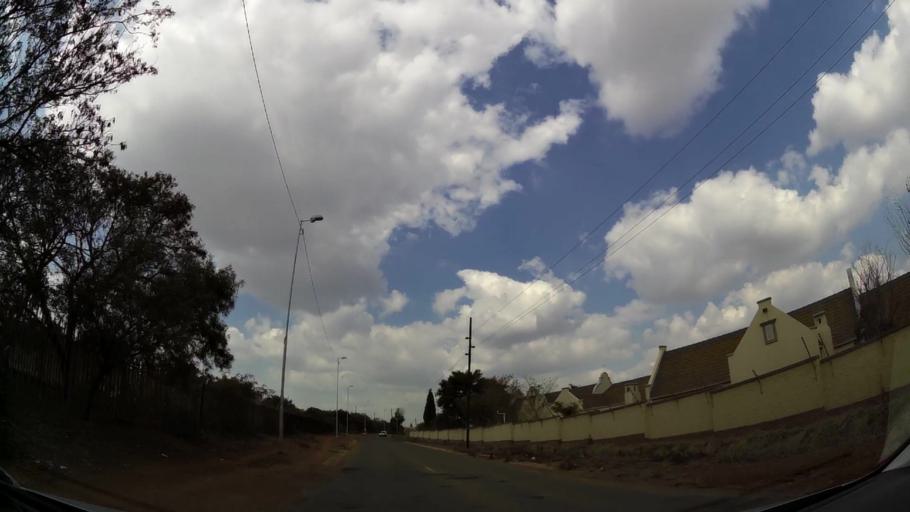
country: ZA
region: Gauteng
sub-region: City of Tshwane Metropolitan Municipality
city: Pretoria
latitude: -25.8028
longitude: 28.3455
